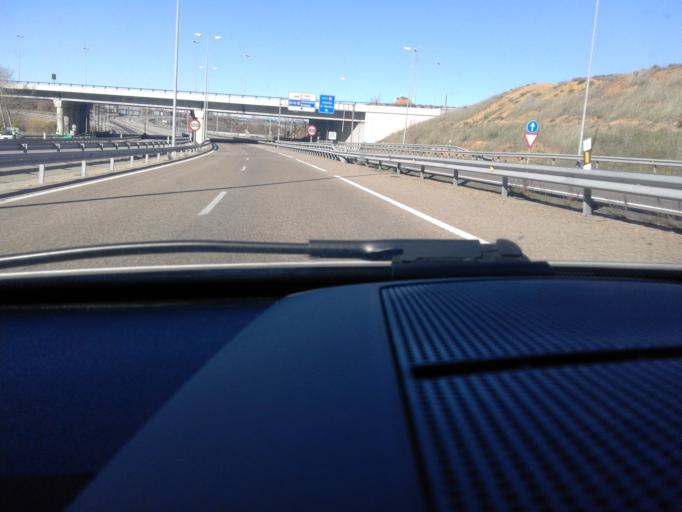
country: ES
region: Castille and Leon
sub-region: Provincia de Leon
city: Valverde de la Virgen
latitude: 42.5674
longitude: -5.6517
